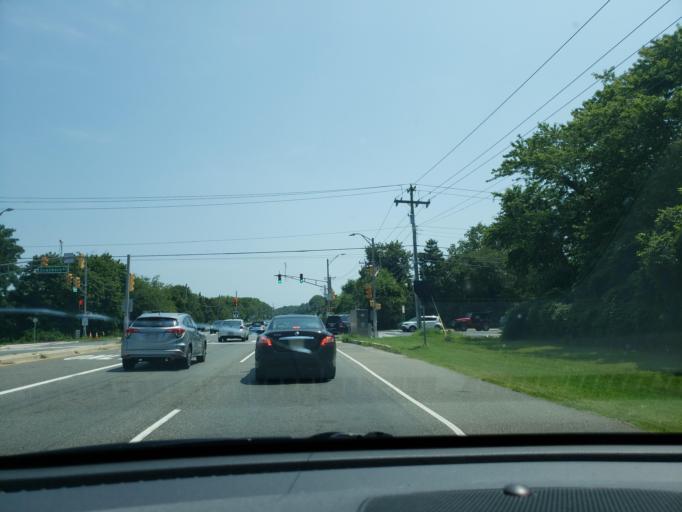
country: US
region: New Jersey
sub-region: Cape May County
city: Erma
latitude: 38.9689
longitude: -74.9219
